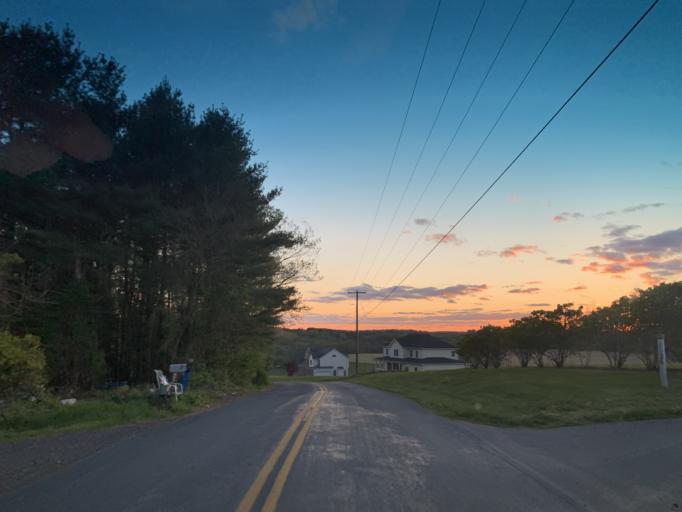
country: US
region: Pennsylvania
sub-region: York County
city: Susquehanna Trails
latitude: 39.6793
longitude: -76.3433
